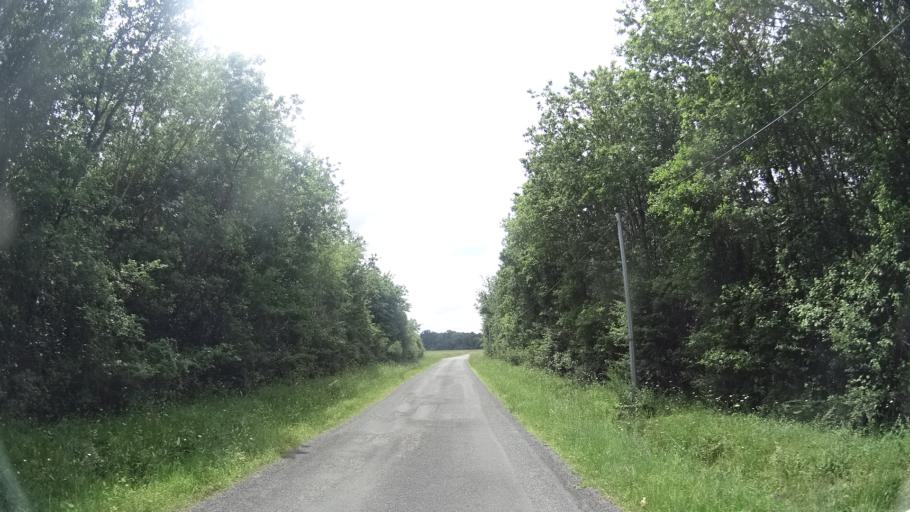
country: FR
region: Pays de la Loire
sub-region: Departement de Maine-et-Loire
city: Chenehutte-Treves-Cunault
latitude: 47.3012
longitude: -0.1535
